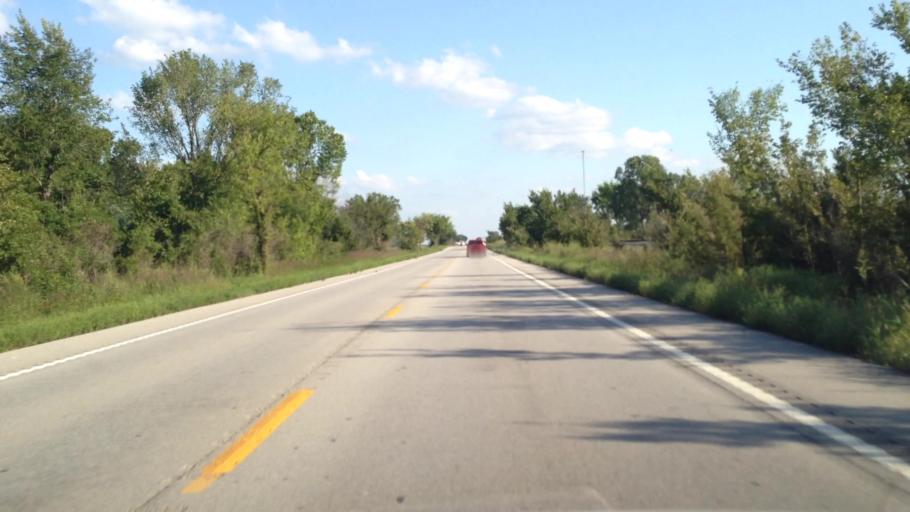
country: US
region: Missouri
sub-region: Jasper County
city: Carl Junction
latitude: 37.2701
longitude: -94.5994
